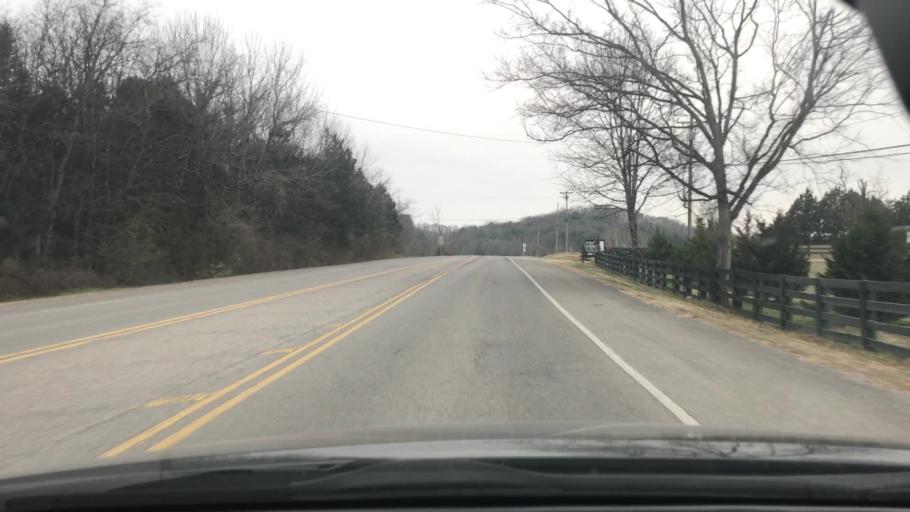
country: US
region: Tennessee
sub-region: Davidson County
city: Forest Hills
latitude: 36.0294
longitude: -86.8621
